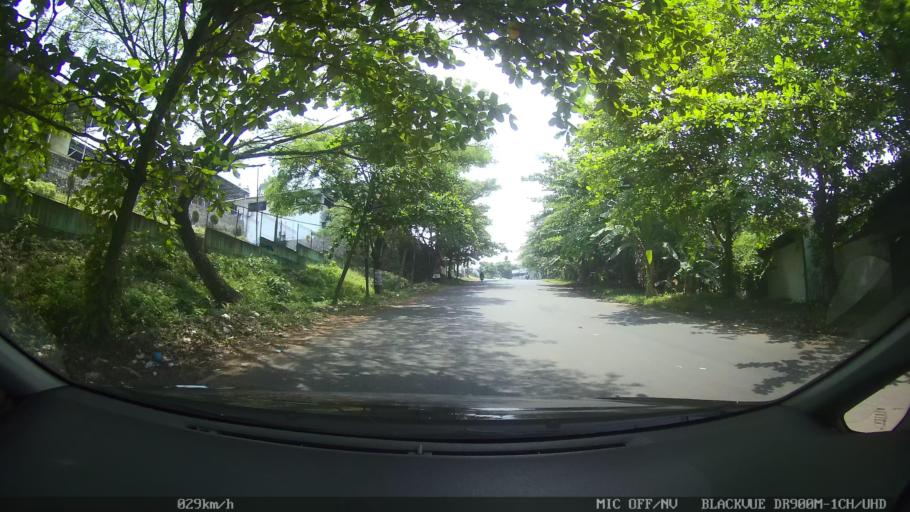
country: ID
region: Lampung
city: Bandarlampung
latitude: -5.4397
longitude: 105.2460
